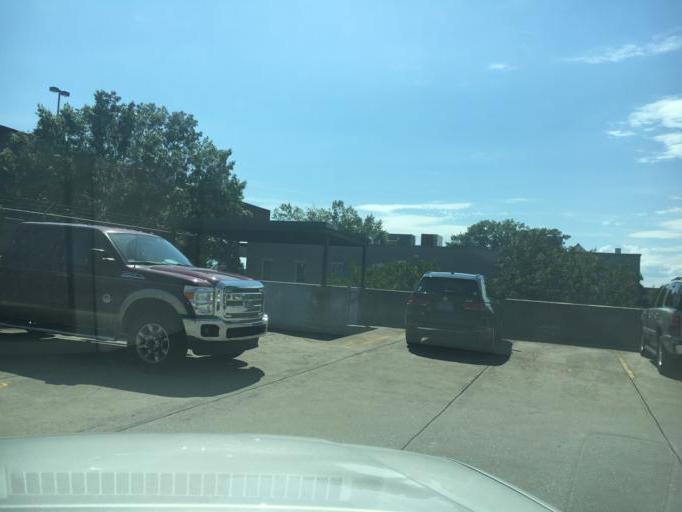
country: US
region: South Carolina
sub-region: Greenville County
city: Greenville
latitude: 34.8530
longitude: -82.3989
